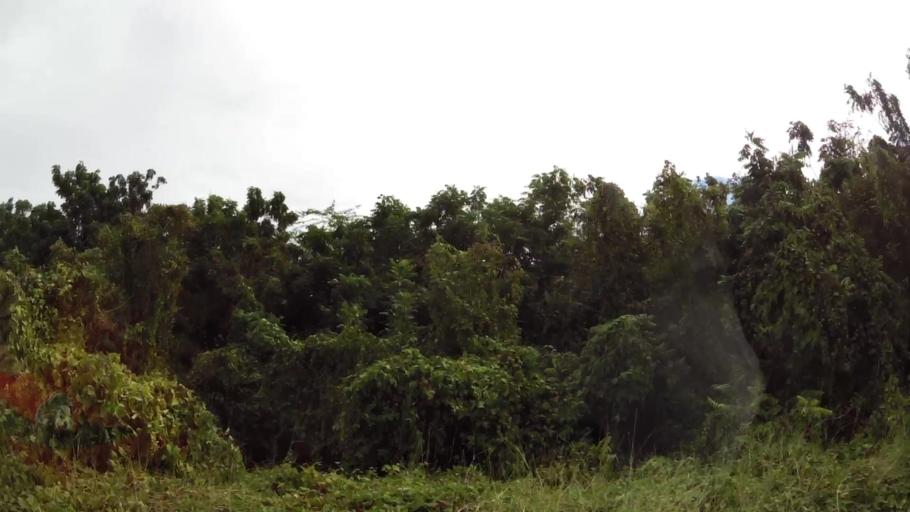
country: AG
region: Saint Paul
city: Falmouth
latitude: 17.0445
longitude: -61.7007
